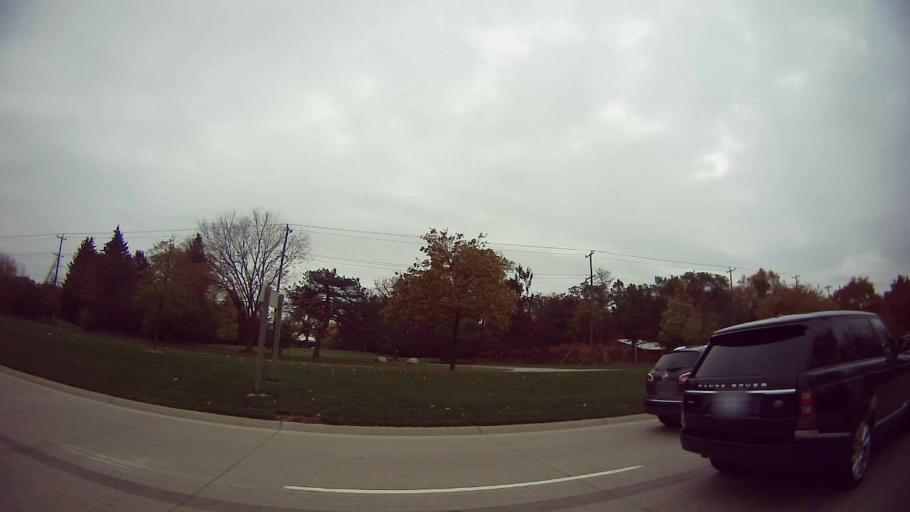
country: US
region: Michigan
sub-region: Oakland County
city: Franklin
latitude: 42.5601
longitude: -83.2856
